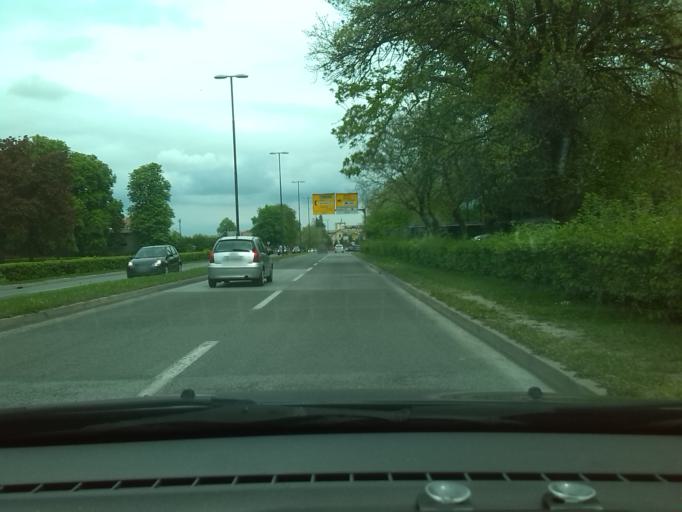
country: SI
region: Ljubljana
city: Ljubljana
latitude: 46.0539
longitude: 14.4990
